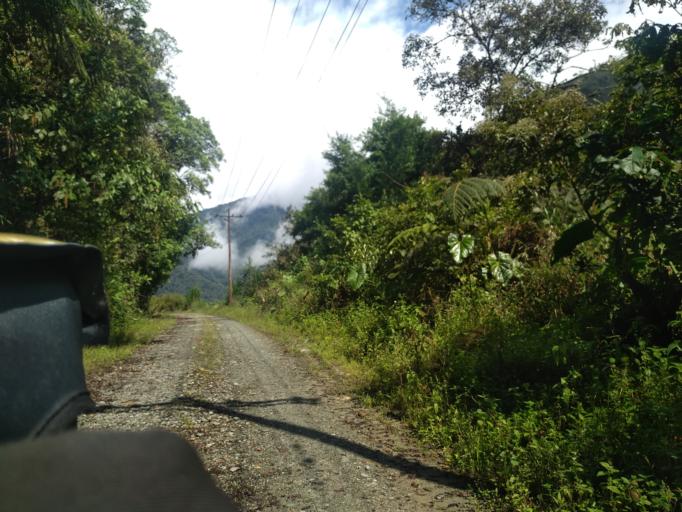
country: EC
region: Tungurahua
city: Banos
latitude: -1.4049
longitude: -78.2806
